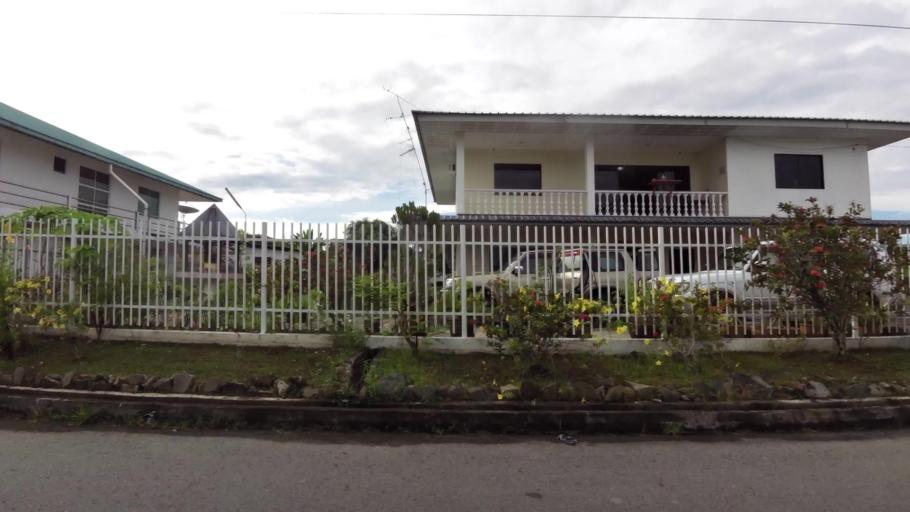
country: BN
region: Belait
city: Seria
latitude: 4.6148
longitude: 114.3610
